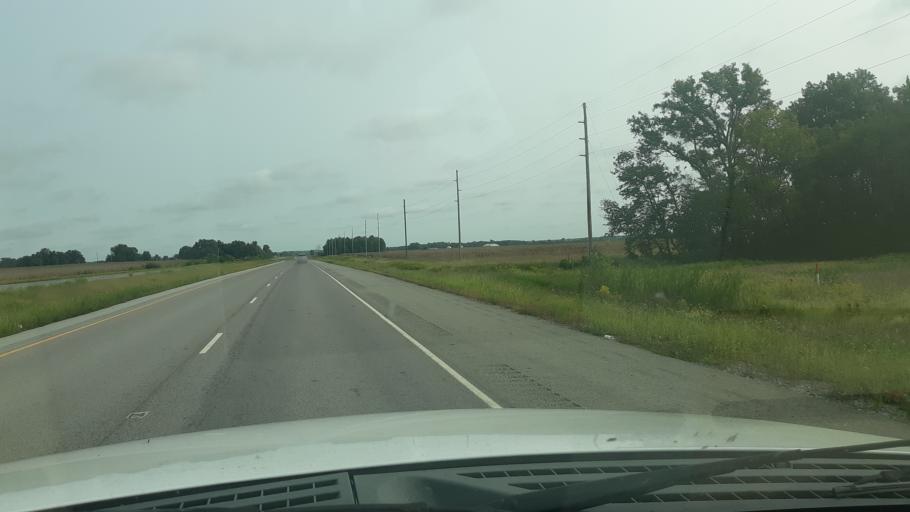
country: US
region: Illinois
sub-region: Saline County
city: Eldorado
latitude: 37.8450
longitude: -88.4129
